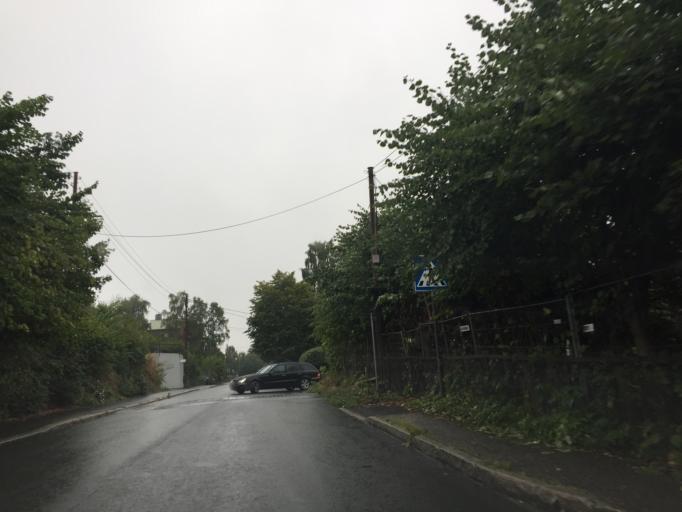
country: NO
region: Oslo
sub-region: Oslo
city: Sjolyststranda
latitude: 59.9490
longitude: 10.6956
